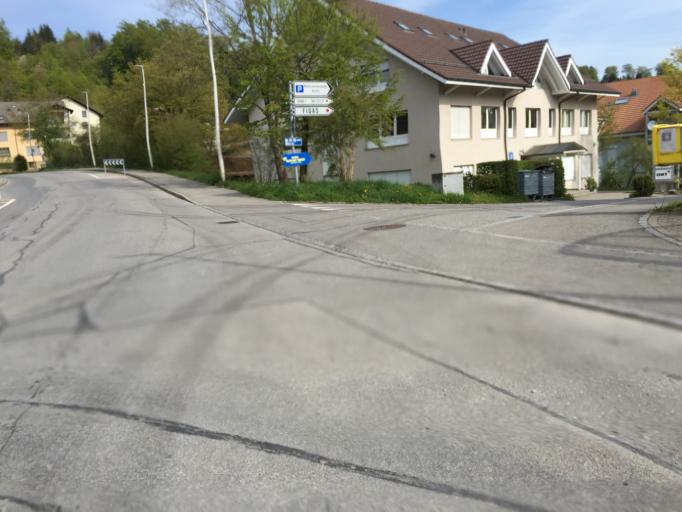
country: CH
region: Bern
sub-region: Bern-Mittelland District
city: Frauenkappelen
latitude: 46.9161
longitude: 7.3618
